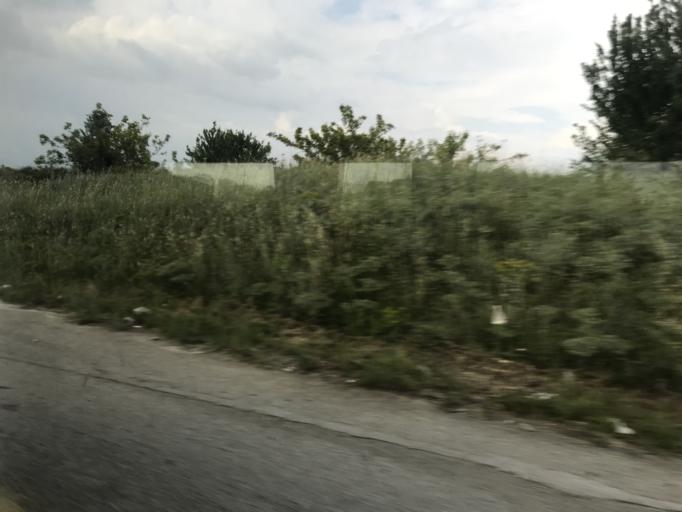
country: GR
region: East Macedonia and Thrace
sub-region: Nomos Rodopis
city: Sapes
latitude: 41.0287
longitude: 25.6858
